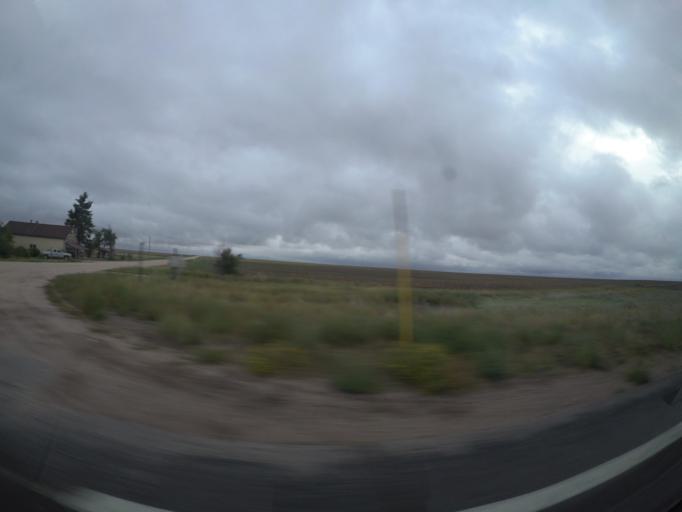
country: US
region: Colorado
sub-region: Washington County
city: Akron
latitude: 39.6993
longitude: -103.0667
